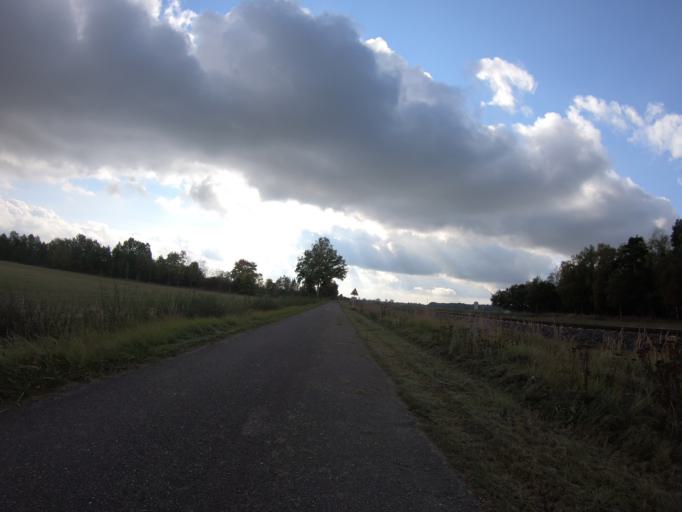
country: DE
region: Lower Saxony
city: Wahrenholz
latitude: 52.5877
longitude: 10.6095
